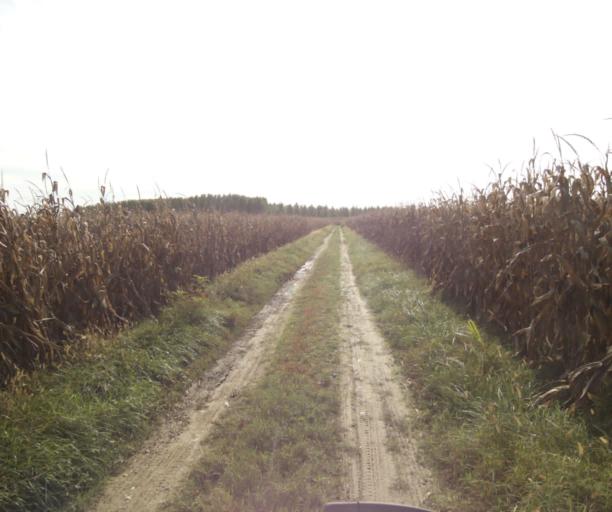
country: FR
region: Midi-Pyrenees
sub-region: Departement du Tarn-et-Garonne
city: Finhan
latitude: 43.9092
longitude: 1.2109
